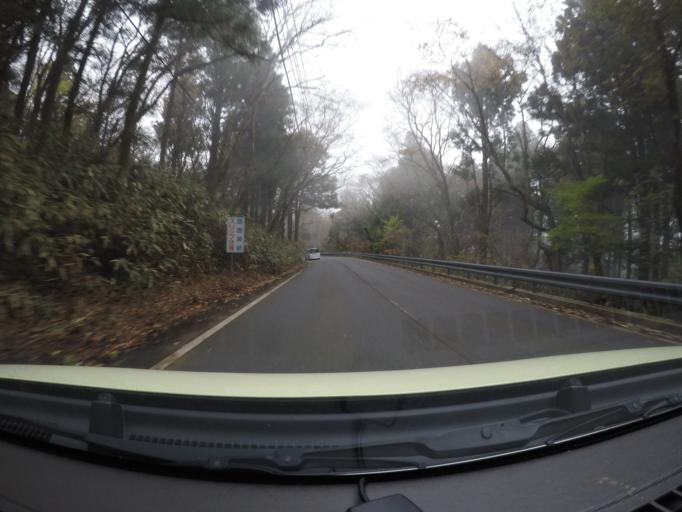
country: JP
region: Kanagawa
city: Hakone
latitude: 35.2474
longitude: 139.0157
